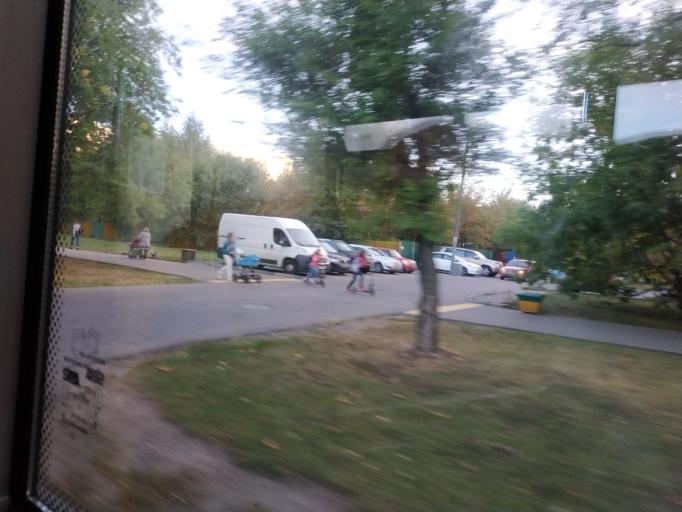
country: RU
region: Moscow
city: Novo-Peredelkino
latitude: 55.6443
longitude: 37.3534
